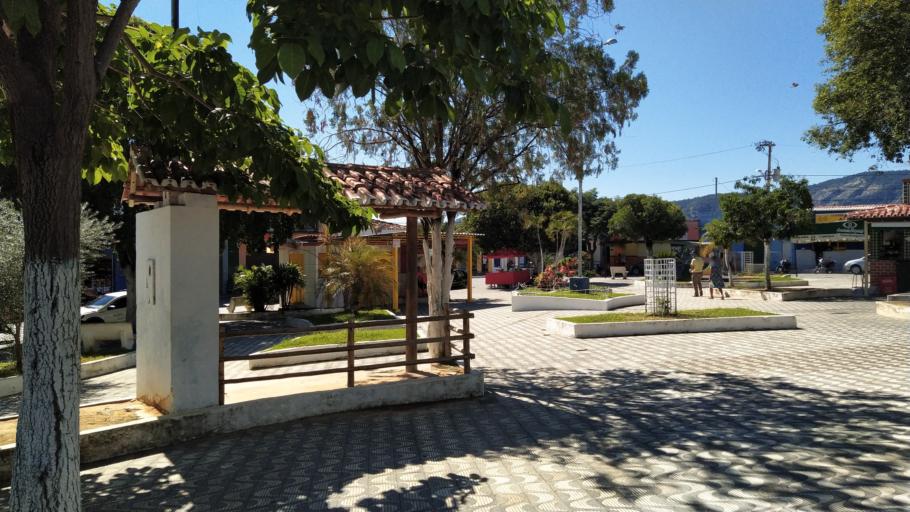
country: BR
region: Minas Gerais
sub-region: Almenara
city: Almenara
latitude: -16.3757
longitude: -40.5391
